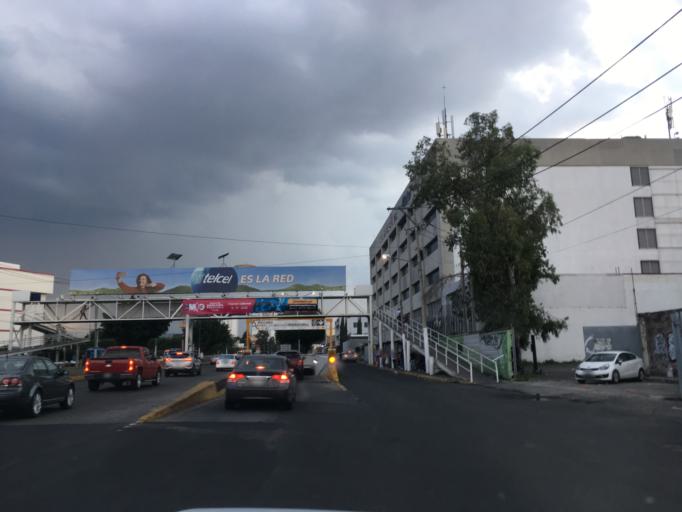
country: MX
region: Jalisco
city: Guadalajara
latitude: 20.6751
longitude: -103.4030
